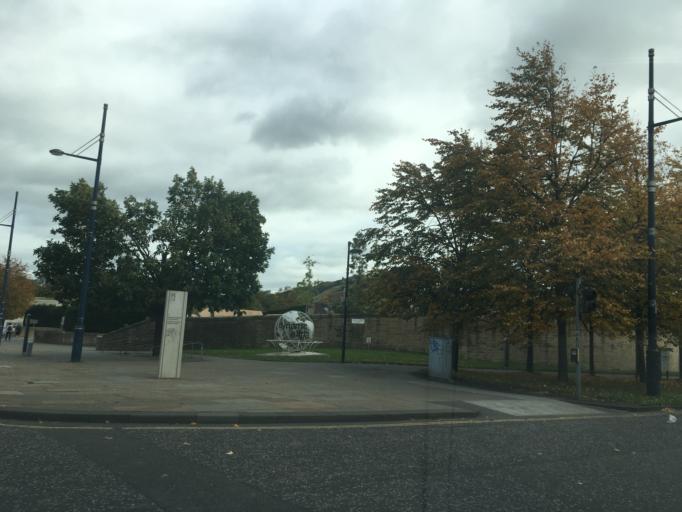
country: GB
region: Scotland
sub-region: Edinburgh
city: Edinburgh
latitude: 55.9510
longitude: -3.1762
